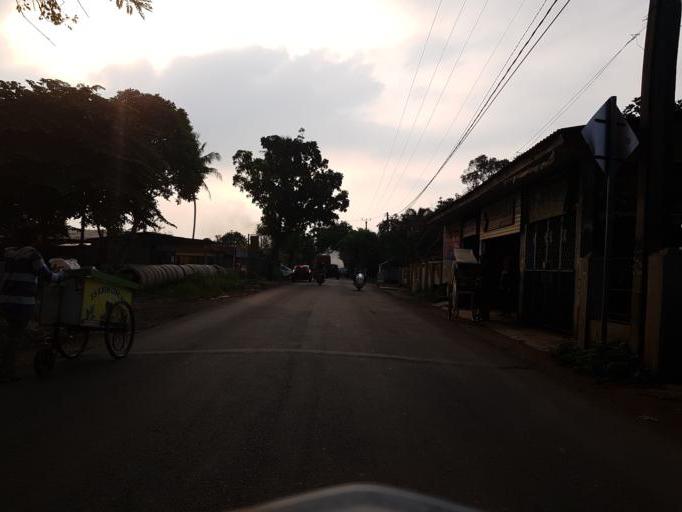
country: ID
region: West Java
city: Parung
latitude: -6.4685
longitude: 106.7143
